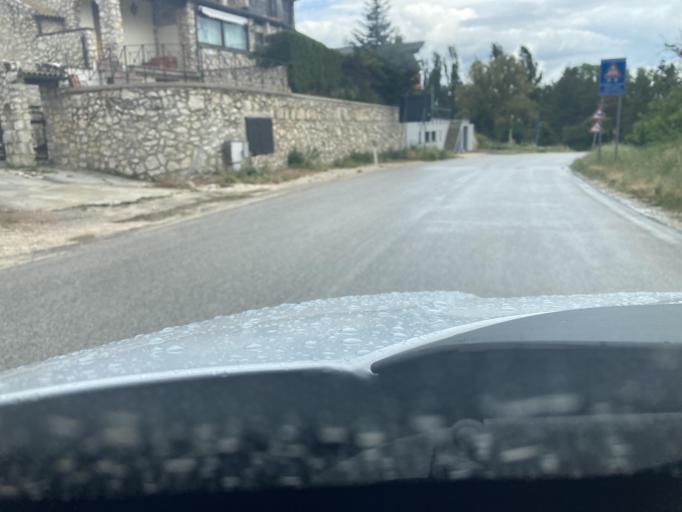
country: IT
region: Abruzzo
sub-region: Provincia dell' Aquila
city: Rocca di Mezzo
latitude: 42.2104
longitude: 13.5183
